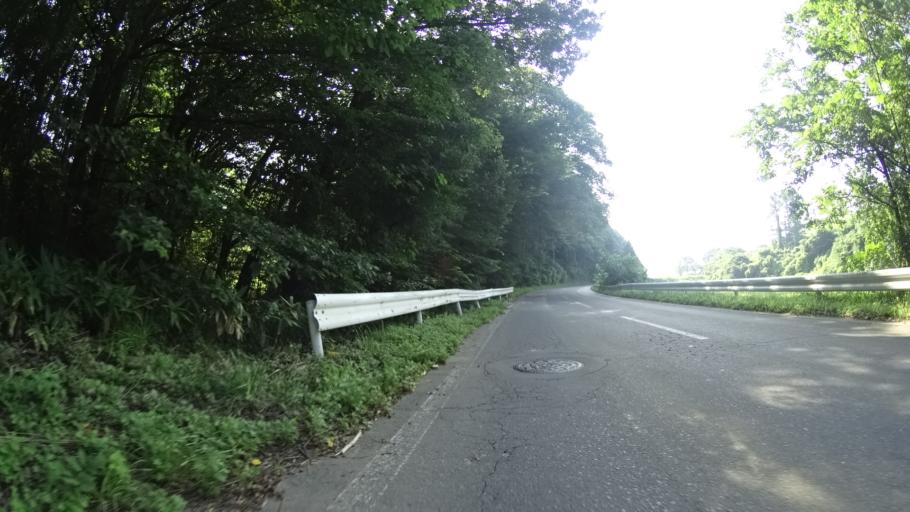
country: JP
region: Nagano
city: Chino
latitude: 35.9735
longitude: 138.1810
